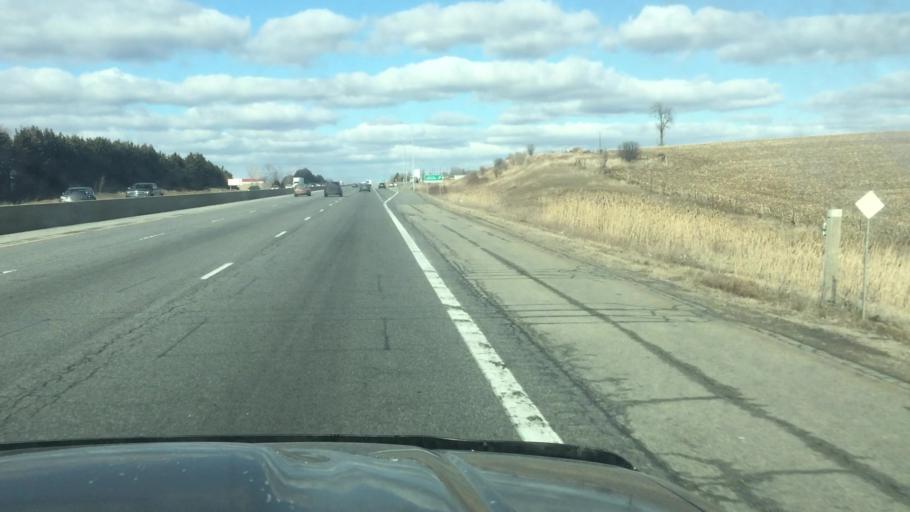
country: CA
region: Ontario
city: Ingersoll
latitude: 43.0624
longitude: -80.8053
